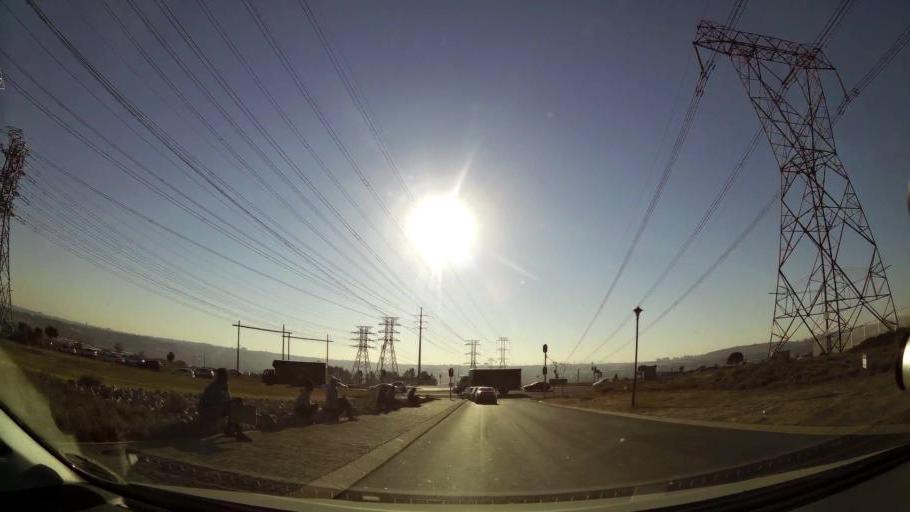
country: ZA
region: Gauteng
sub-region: City of Johannesburg Metropolitan Municipality
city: Modderfontein
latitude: -26.0435
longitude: 28.1479
